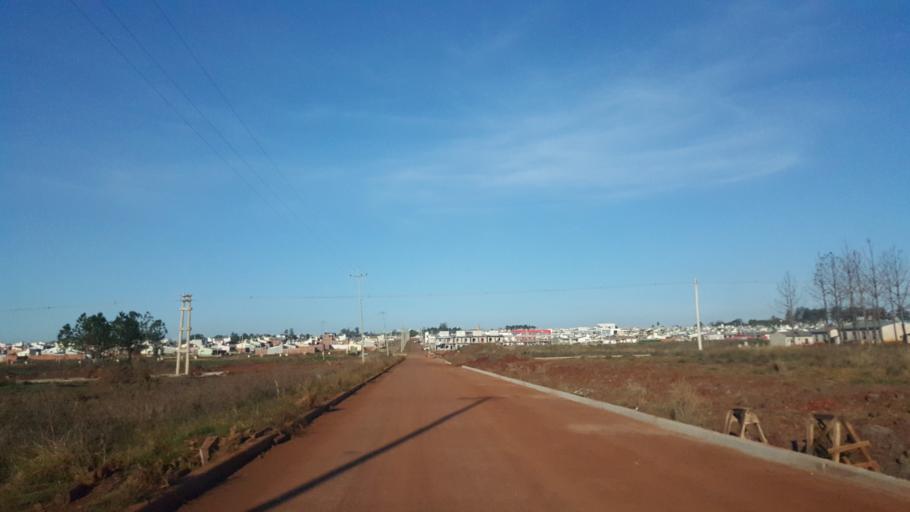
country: AR
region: Misiones
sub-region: Departamento de Capital
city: Posadas
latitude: -27.4069
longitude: -55.9908
